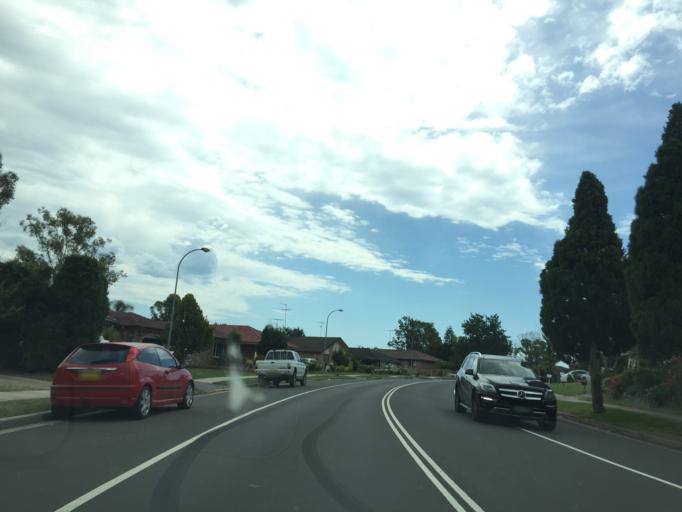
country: AU
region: New South Wales
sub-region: Blacktown
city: Mount Druitt
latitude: -33.8059
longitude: 150.7908
